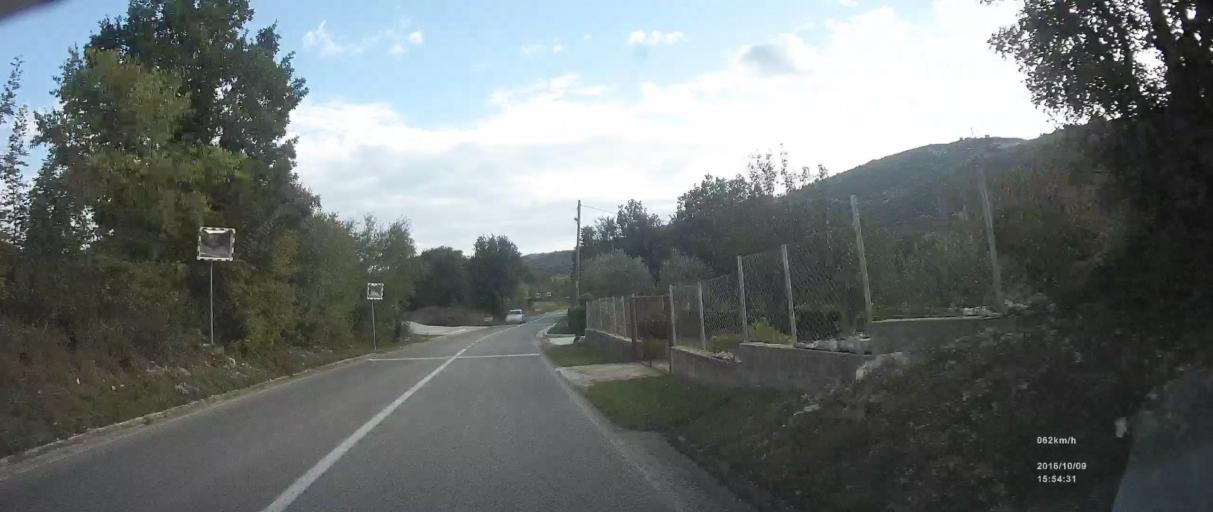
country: HR
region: Splitsko-Dalmatinska
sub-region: Grad Trogir
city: Trogir
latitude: 43.5941
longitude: 16.2256
